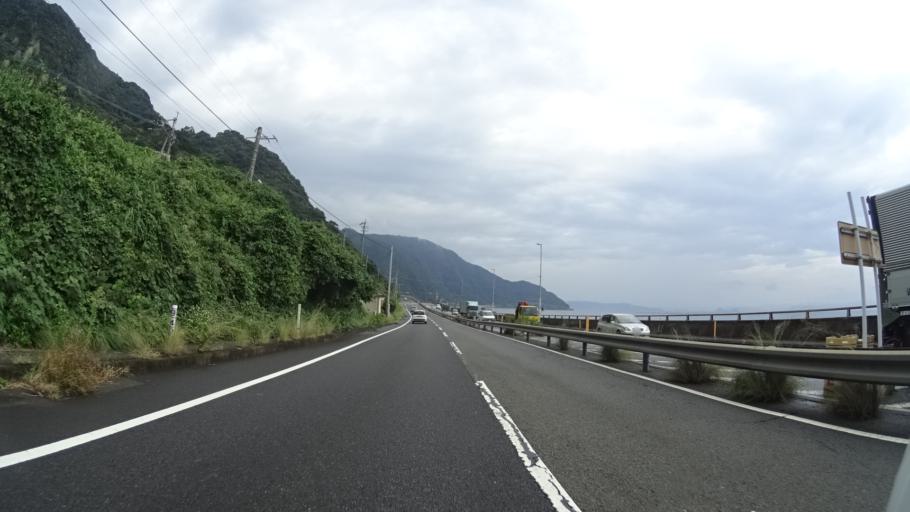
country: JP
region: Kagoshima
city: Kagoshima-shi
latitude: 31.6347
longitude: 130.6018
